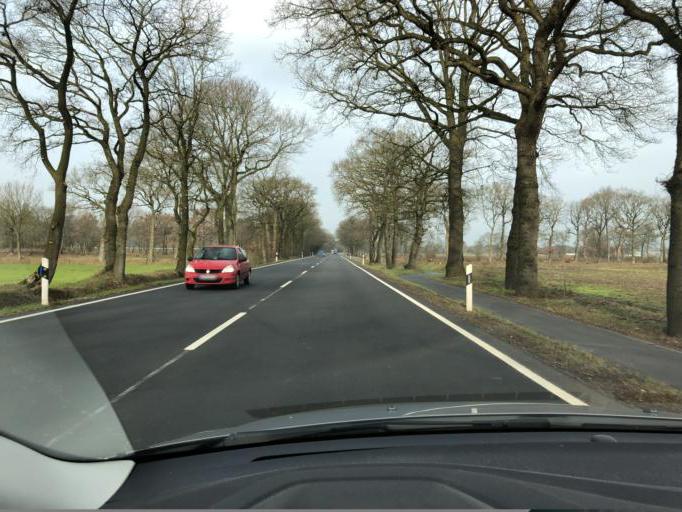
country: DE
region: Lower Saxony
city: Mittegrossefehn
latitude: 53.3662
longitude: 7.5907
